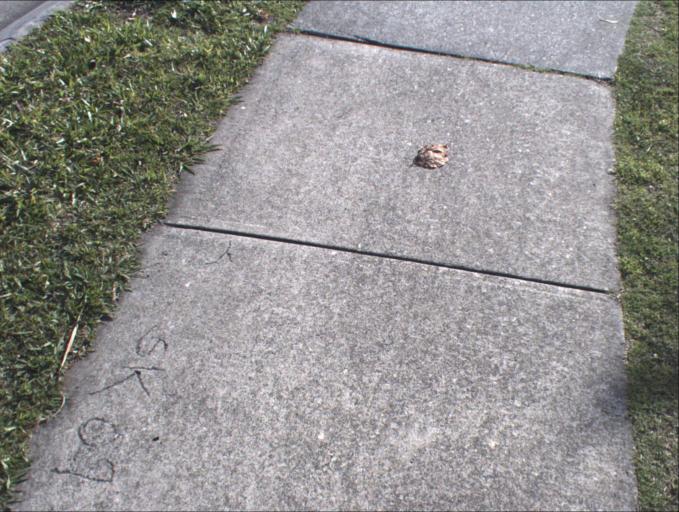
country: AU
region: Queensland
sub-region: Logan
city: Waterford West
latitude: -27.6807
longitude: 153.1172
